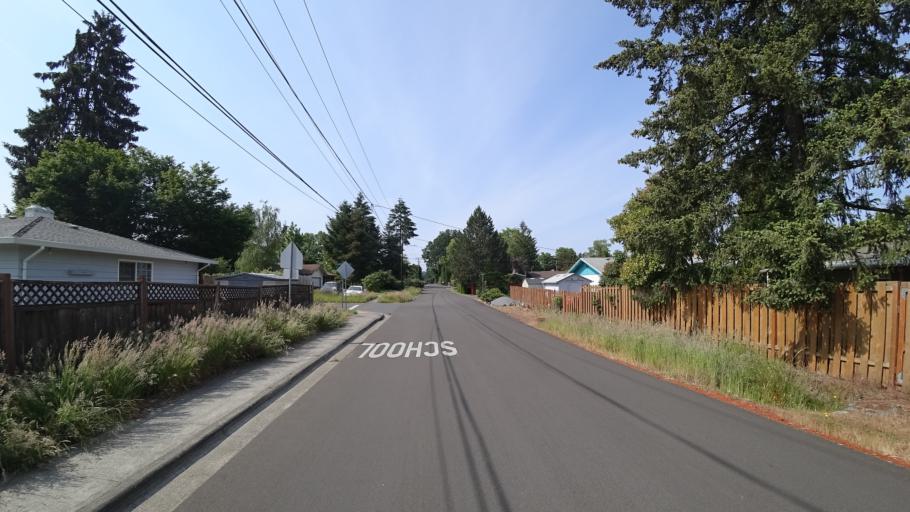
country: US
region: Oregon
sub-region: Washington County
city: Cedar Hills
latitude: 45.5048
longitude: -122.8191
